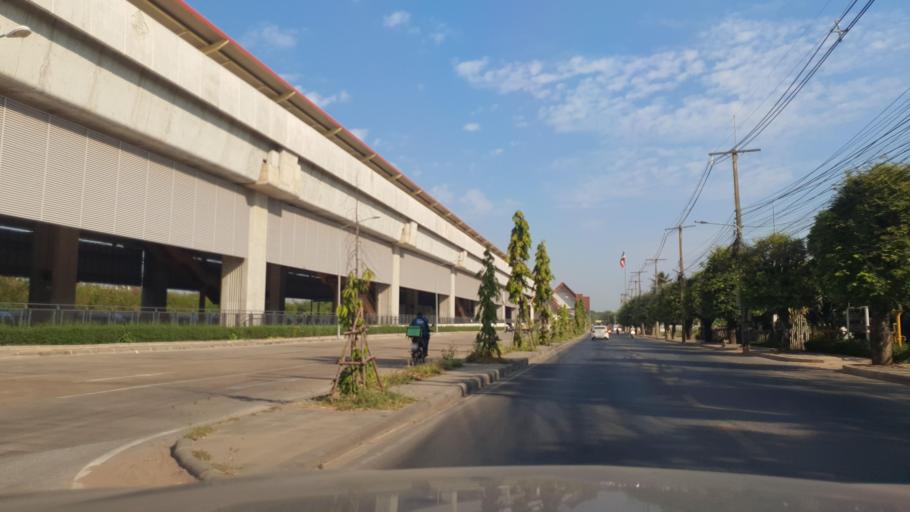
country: TH
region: Khon Kaen
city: Khon Kaen
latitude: 16.4244
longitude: 102.8252
